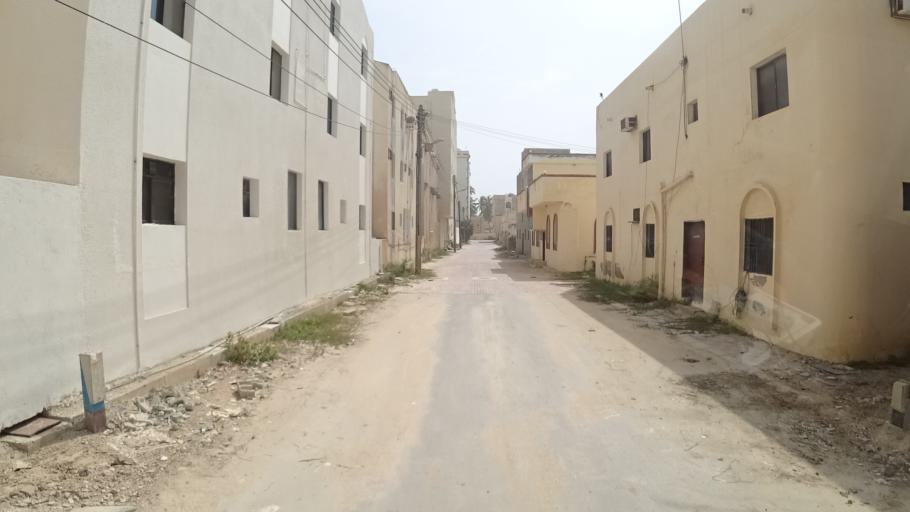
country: OM
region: Zufar
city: Salalah
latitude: 17.0092
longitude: 54.1593
